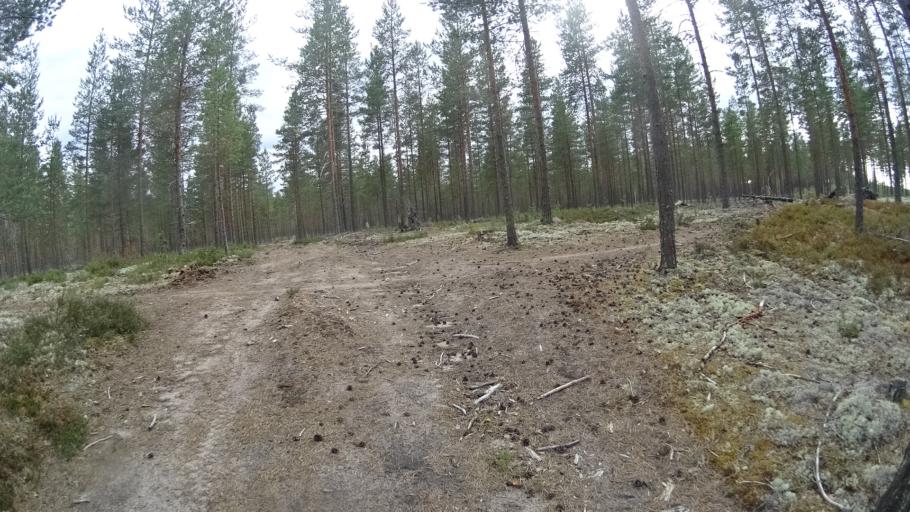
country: FI
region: Satakunta
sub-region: Pohjois-Satakunta
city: Jaemijaervi
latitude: 61.7715
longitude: 22.8046
